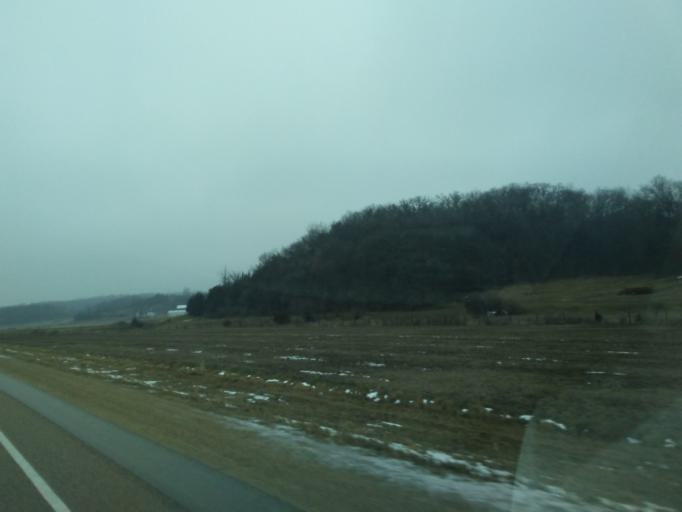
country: US
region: Wisconsin
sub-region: Dane County
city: Cross Plains
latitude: 43.1238
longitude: -89.7015
